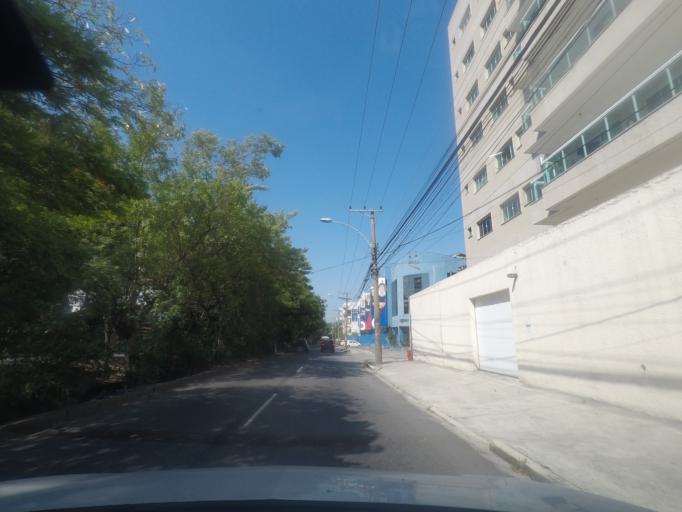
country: BR
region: Rio de Janeiro
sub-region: Sao Joao De Meriti
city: Sao Joao de Meriti
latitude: -22.8836
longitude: -43.3728
